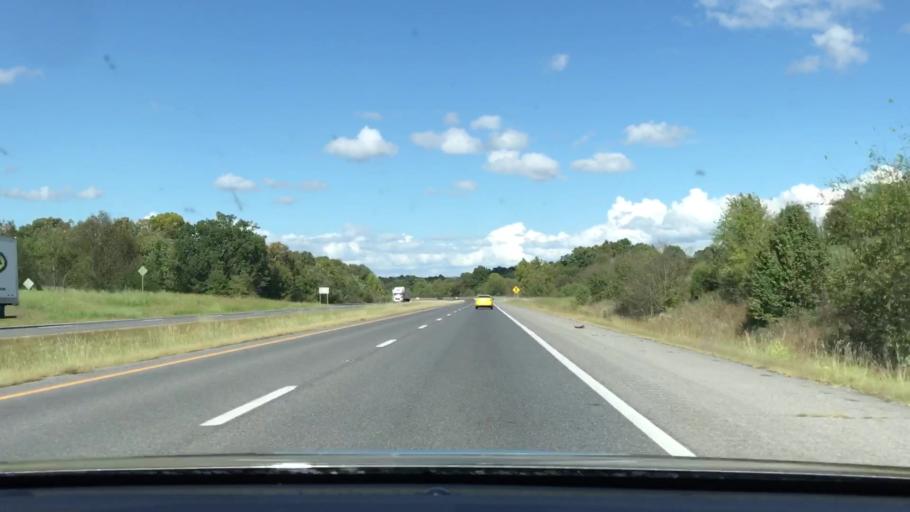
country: US
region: Kentucky
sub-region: Marshall County
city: Benton
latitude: 36.9289
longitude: -88.3456
